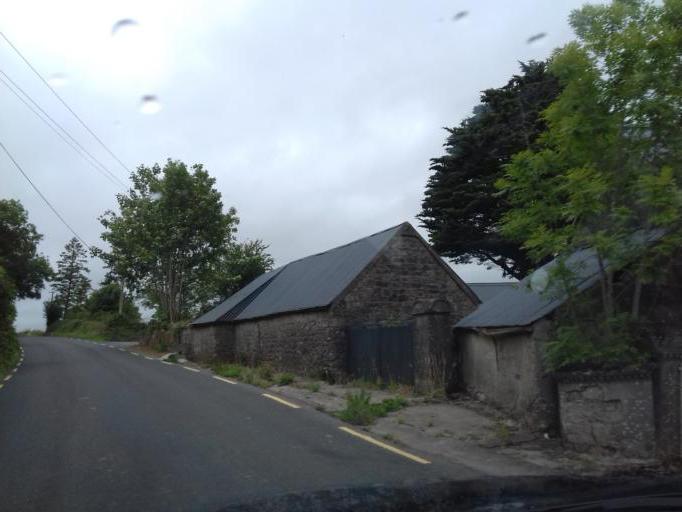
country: IE
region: Leinster
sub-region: Kilkenny
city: Graiguenamanagh
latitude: 52.6060
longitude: -7.0198
